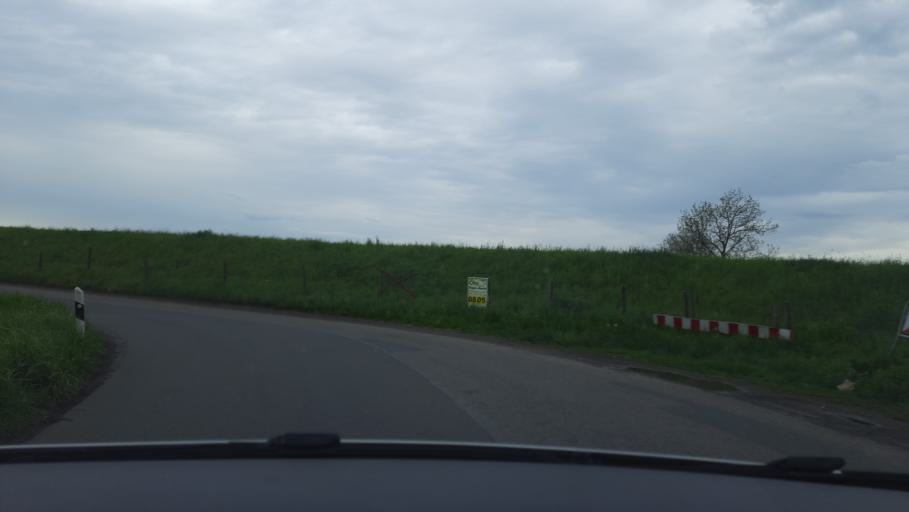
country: DE
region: Lower Saxony
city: Thedinghausen
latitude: 52.9826
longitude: 9.0435
